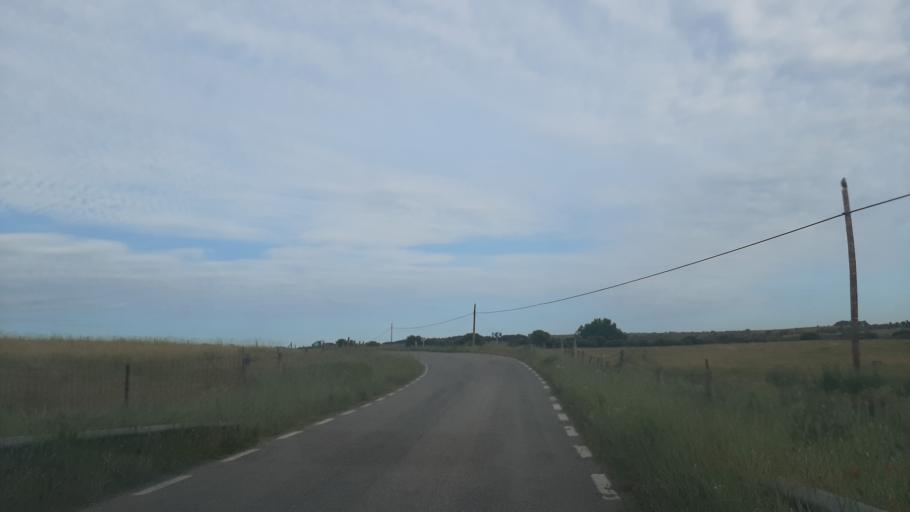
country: ES
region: Castille and Leon
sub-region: Provincia de Salamanca
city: Gallegos de Arganan
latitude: 40.6360
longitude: -6.7168
